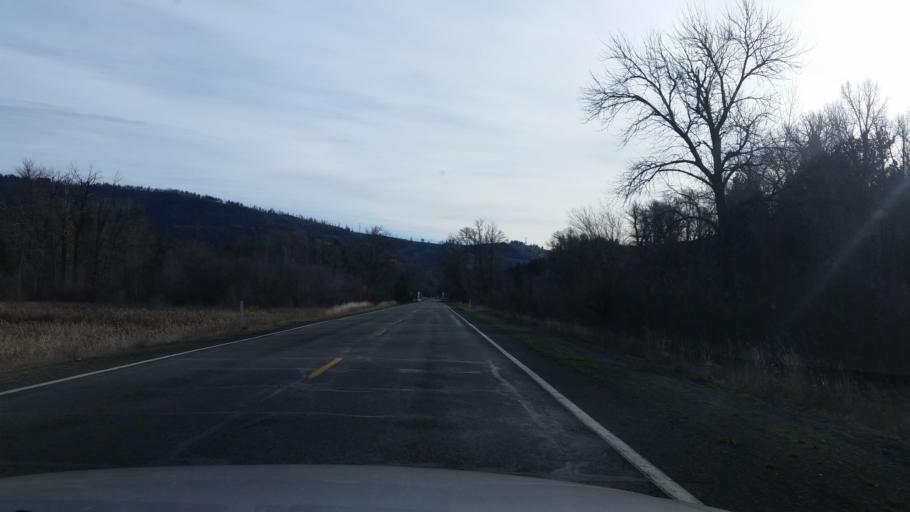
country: US
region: Washington
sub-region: Kittitas County
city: Cle Elum
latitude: 47.1695
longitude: -120.8377
